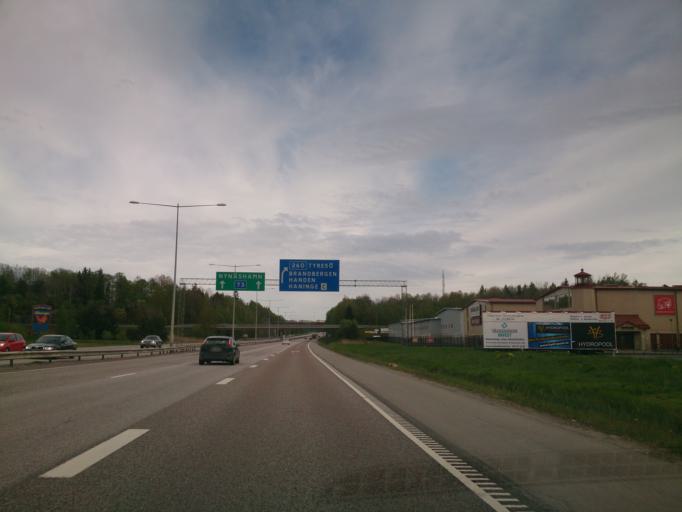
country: SE
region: Stockholm
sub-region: Haninge Kommun
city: Haninge
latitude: 59.1864
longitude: 18.1489
